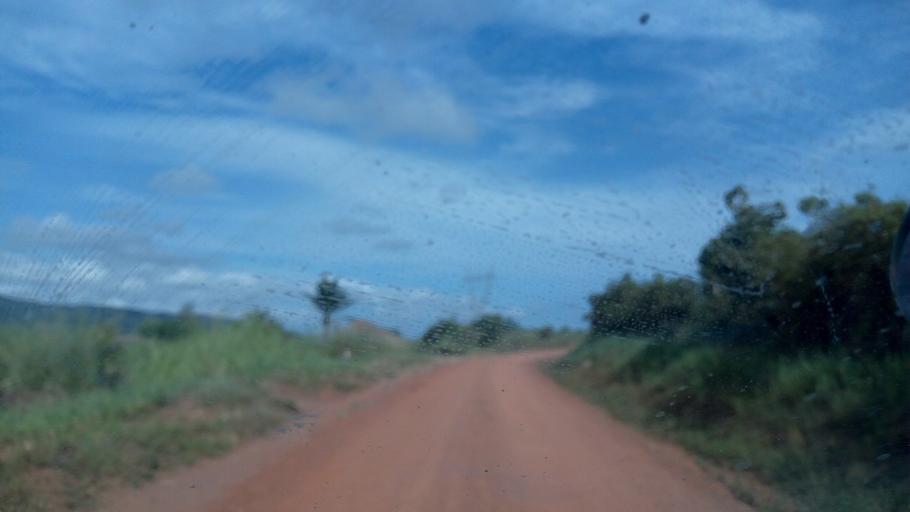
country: CD
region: Katanga
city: Kalemie
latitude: -5.7824
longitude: 29.1137
